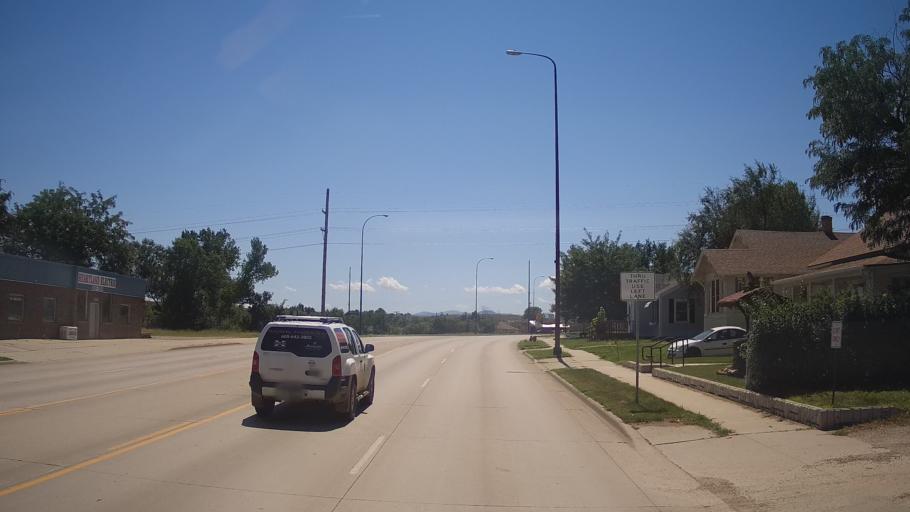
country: US
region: South Dakota
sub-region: Butte County
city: Belle Fourche
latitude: 44.6654
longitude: -103.8538
